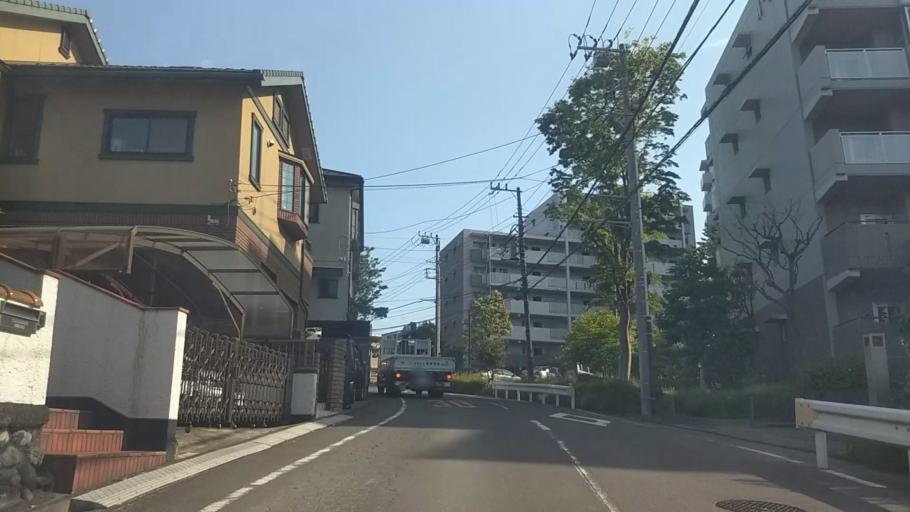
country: JP
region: Kanagawa
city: Fujisawa
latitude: 35.3453
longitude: 139.4900
